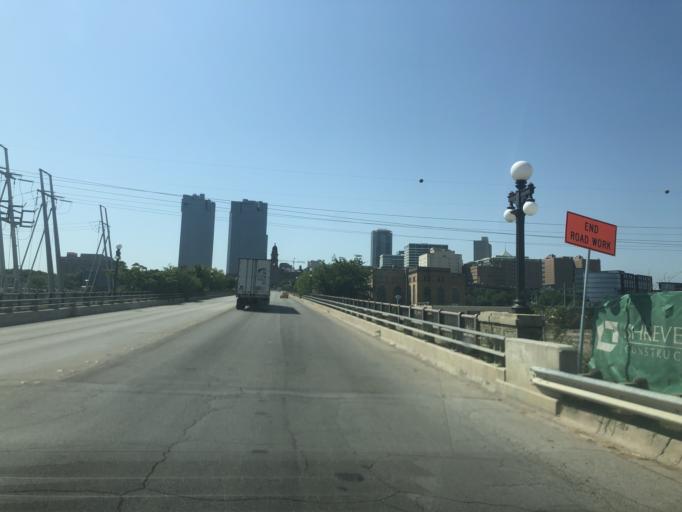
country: US
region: Texas
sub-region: Tarrant County
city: Fort Worth
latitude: 32.7628
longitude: -97.3368
